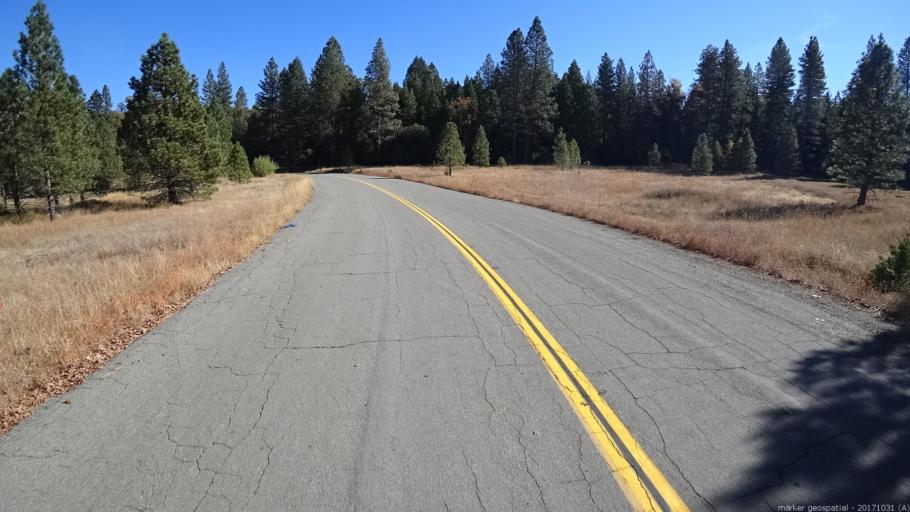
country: US
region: California
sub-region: Shasta County
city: Shingletown
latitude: 40.4908
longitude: -121.8848
